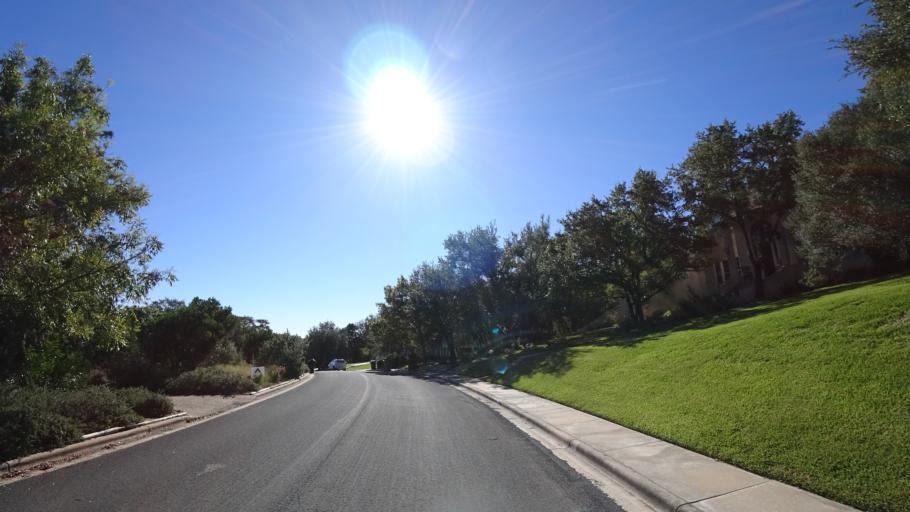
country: US
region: Texas
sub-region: Travis County
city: West Lake Hills
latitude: 30.3290
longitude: -97.7918
